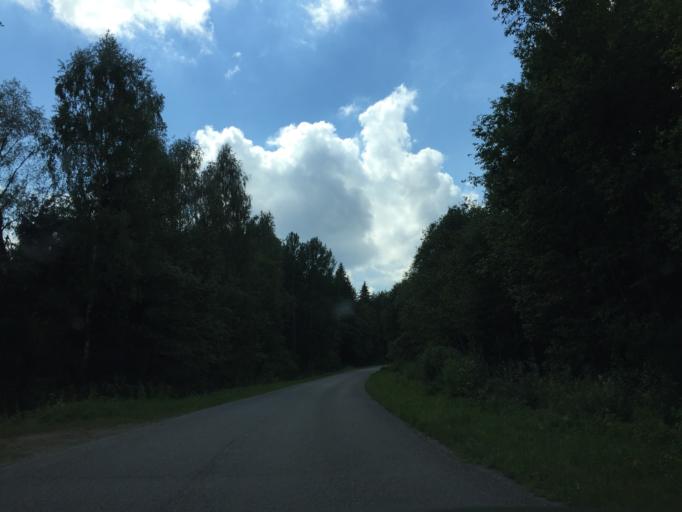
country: LV
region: Ligatne
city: Ligatne
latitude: 57.2504
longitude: 25.0768
